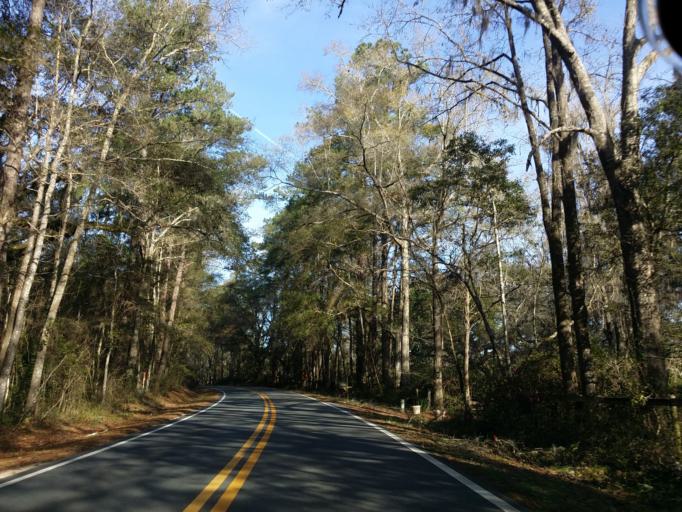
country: US
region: Florida
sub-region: Leon County
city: Woodville
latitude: 30.3949
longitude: -84.1560
